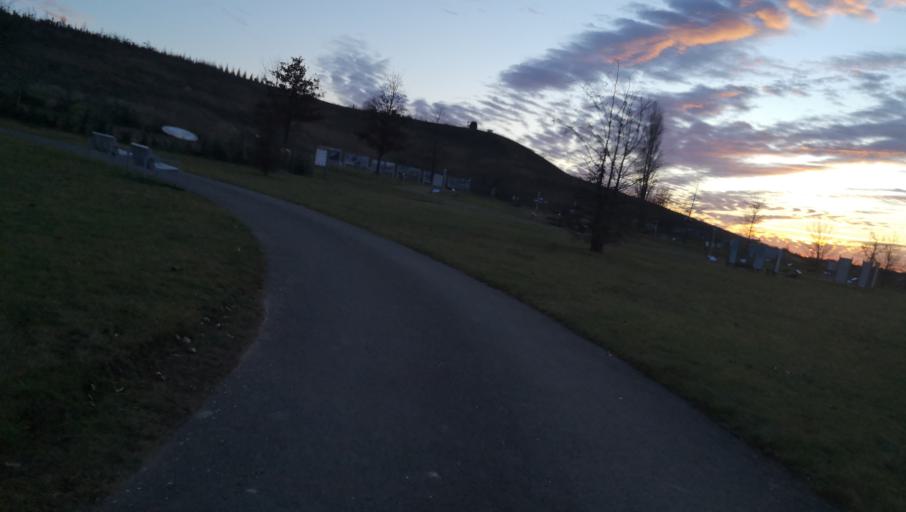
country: DE
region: Thuringia
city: Ronneburg
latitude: 50.8563
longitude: 12.1739
